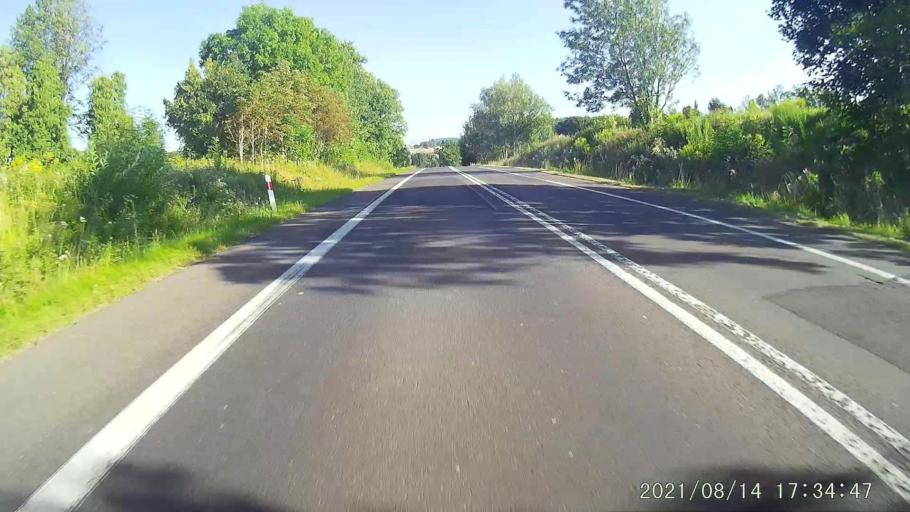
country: PL
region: Lower Silesian Voivodeship
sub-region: Powiat jeleniogorski
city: Stara Kamienica
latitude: 50.9398
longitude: 15.5947
